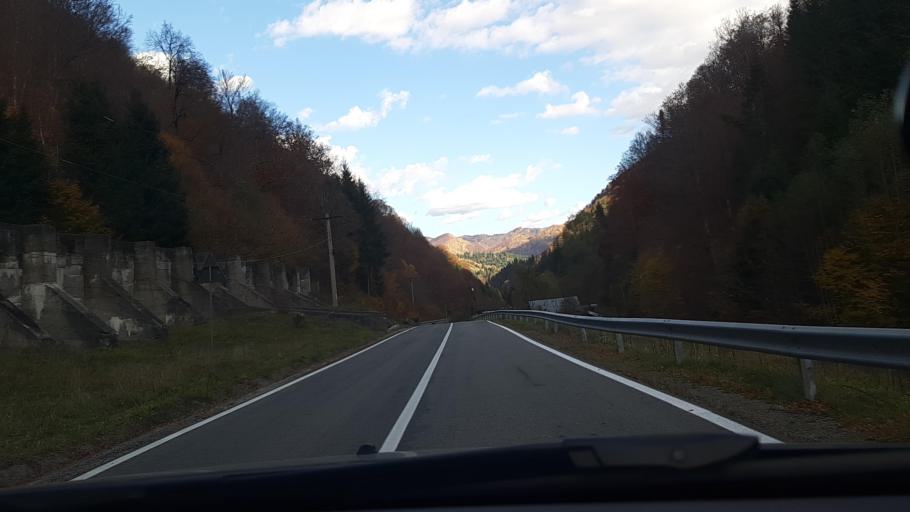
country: RO
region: Valcea
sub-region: Comuna Voineasa
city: Voineasa
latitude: 45.4236
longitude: 23.9285
